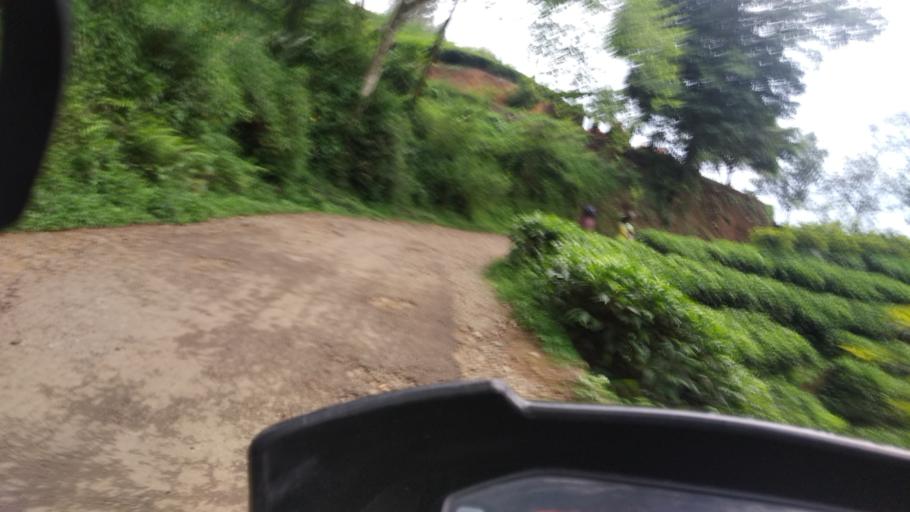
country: IN
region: Tamil Nadu
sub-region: Theni
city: Gudalur
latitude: 9.5550
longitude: 77.0632
